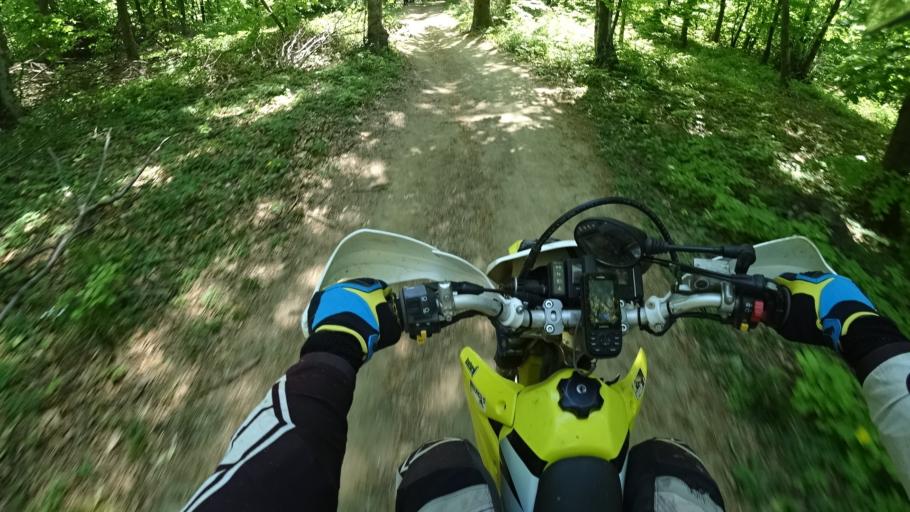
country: HR
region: Zagrebacka
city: Jablanovec
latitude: 45.8644
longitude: 15.8694
